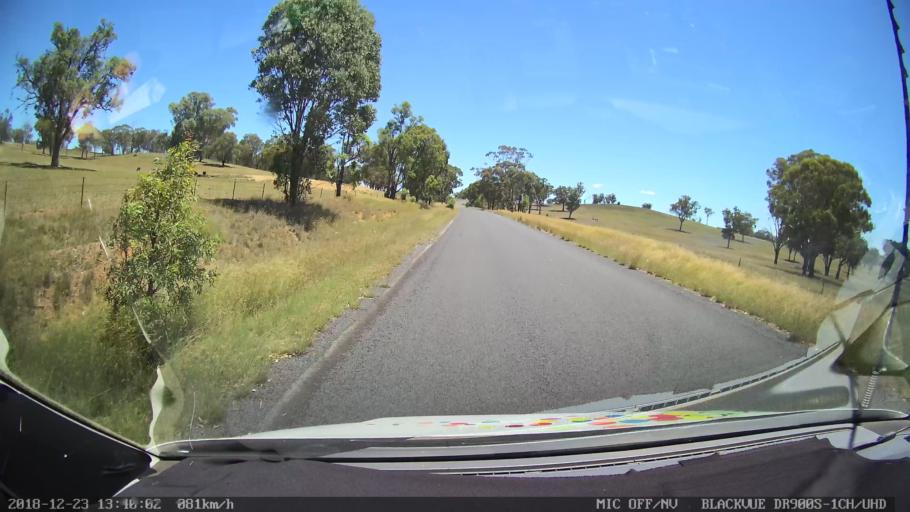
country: AU
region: New South Wales
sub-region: Armidale Dumaresq
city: Armidale
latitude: -30.4633
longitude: 151.1954
